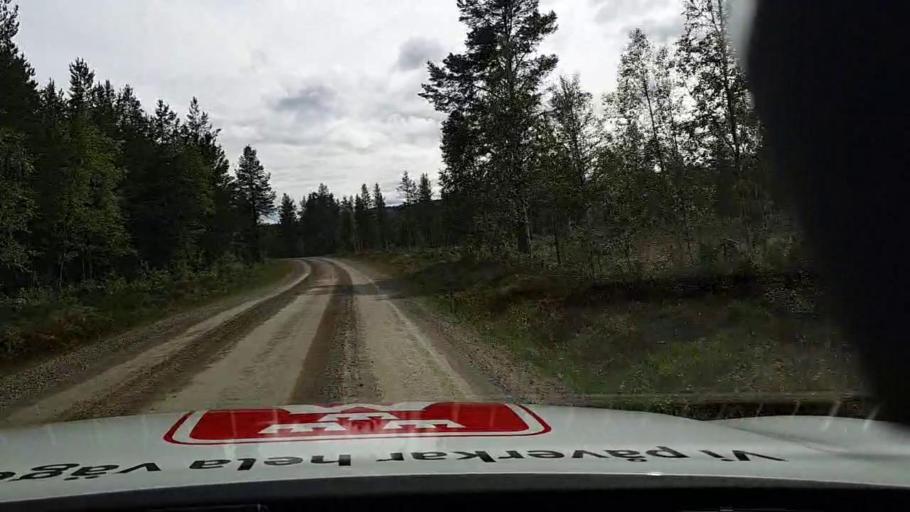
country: SE
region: Jaemtland
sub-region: Are Kommun
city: Jarpen
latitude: 62.5002
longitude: 13.5015
